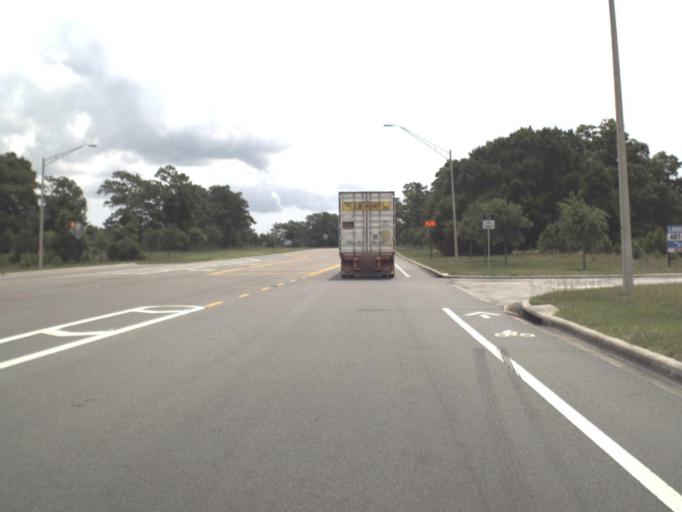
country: US
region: Florida
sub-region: Duval County
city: Jacksonville
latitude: 30.4301
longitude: -81.6436
